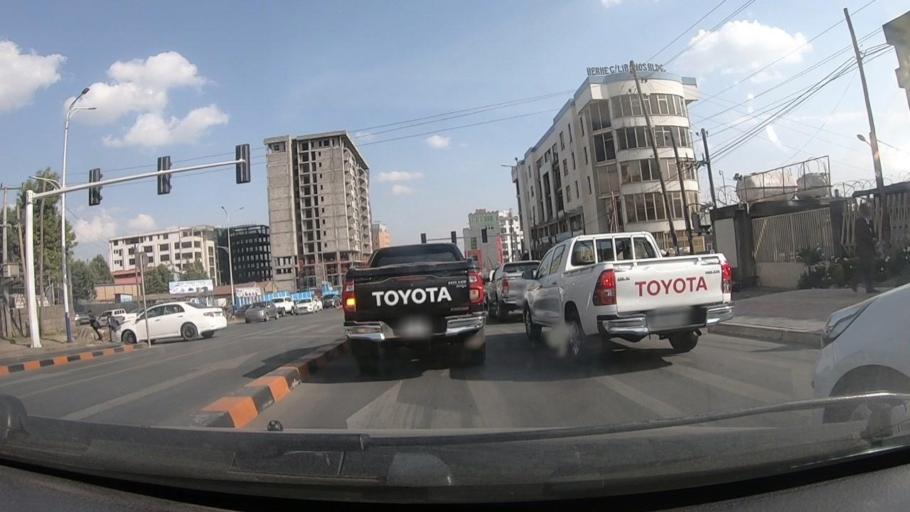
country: ET
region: Adis Abeba
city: Addis Ababa
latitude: 8.9903
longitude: 38.7415
